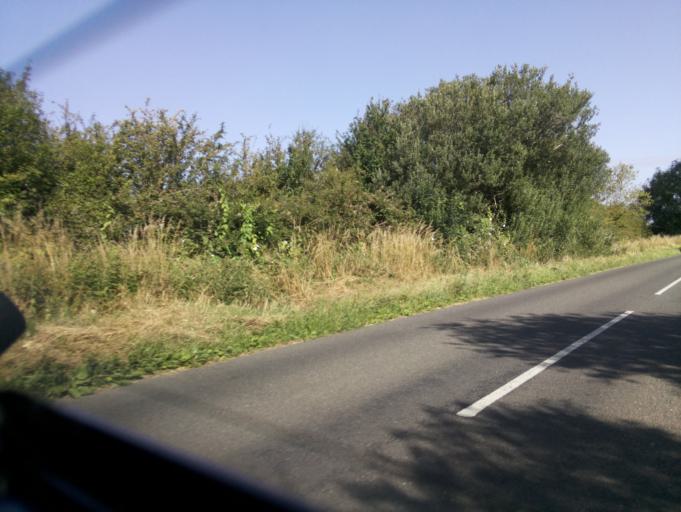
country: GB
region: England
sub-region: Oxfordshire
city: Bampton
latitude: 51.7067
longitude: -1.5204
